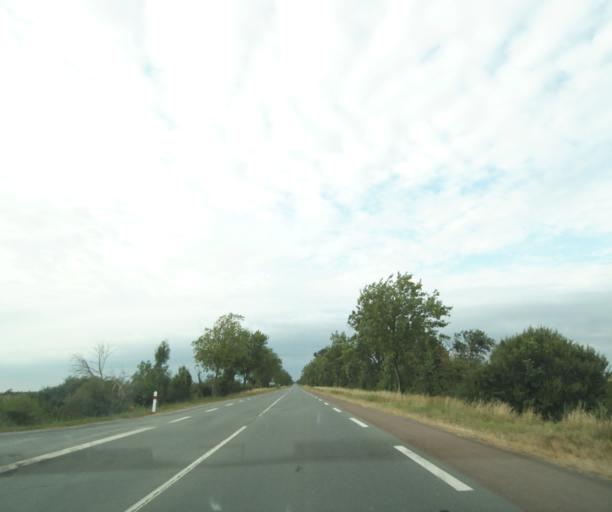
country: FR
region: Poitou-Charentes
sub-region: Departement de la Charente-Maritime
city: Marans
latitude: 46.2856
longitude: -0.9935
